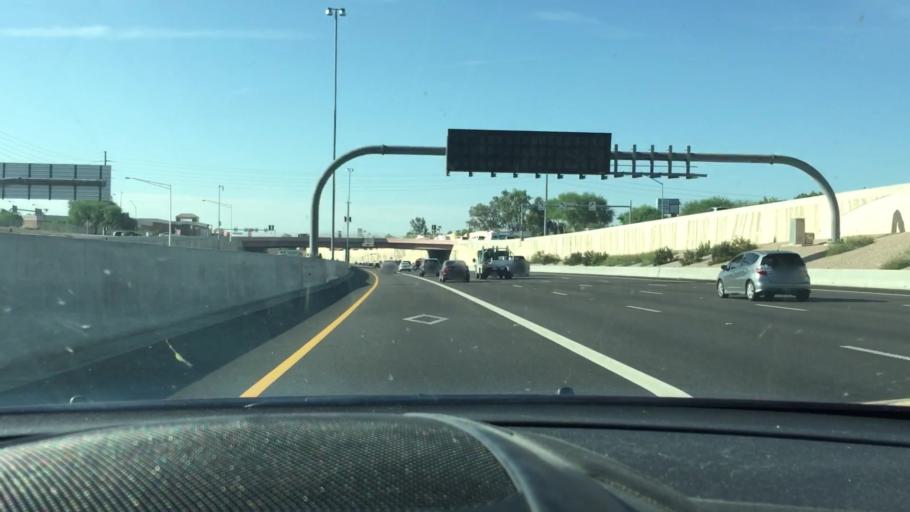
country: US
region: Arizona
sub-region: Maricopa County
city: Paradise Valley
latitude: 33.5844
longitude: -111.8923
